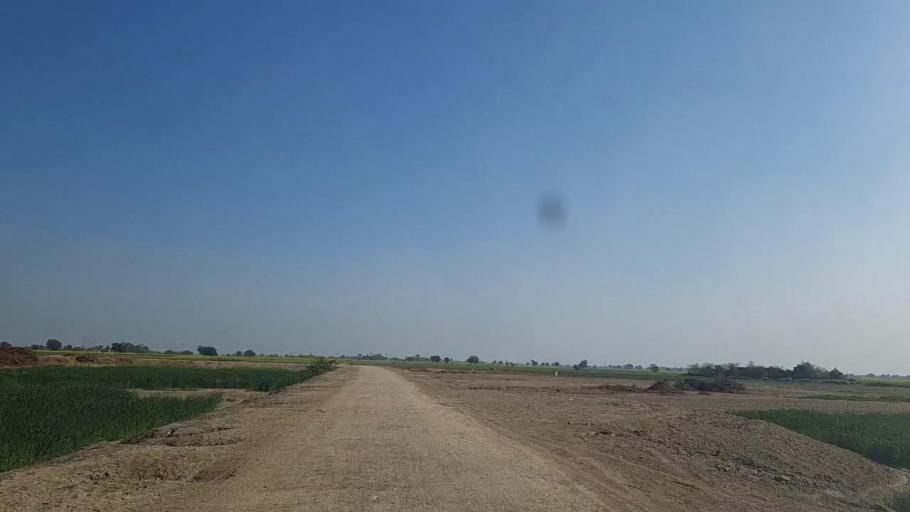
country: PK
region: Sindh
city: Shahpur Chakar
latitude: 26.1962
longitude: 68.5941
